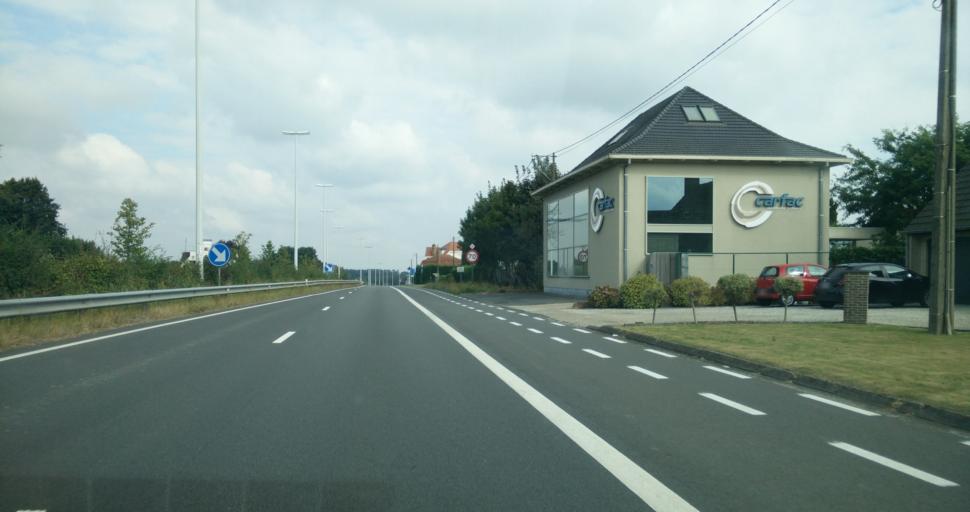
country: BE
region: Flanders
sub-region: Provincie Oost-Vlaanderen
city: Ronse
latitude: 50.7937
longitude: 3.5910
